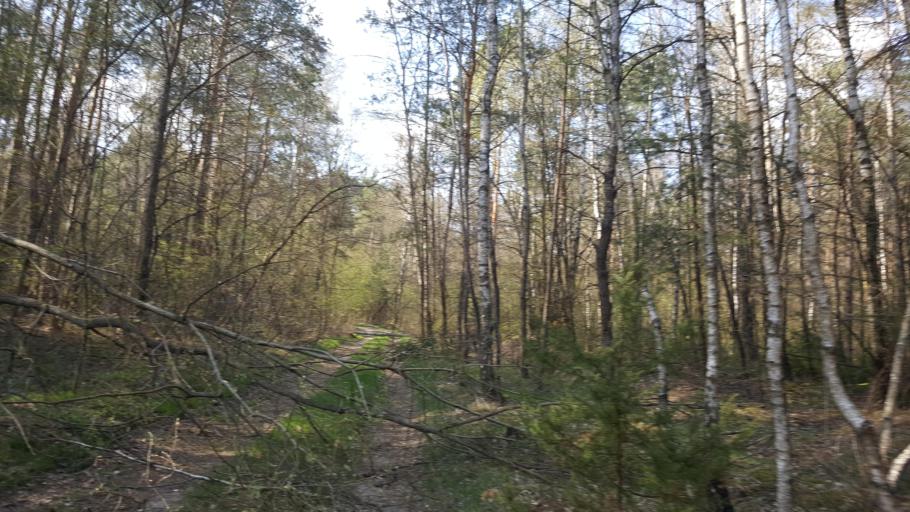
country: BY
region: Brest
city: Kamyanyets
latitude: 52.3441
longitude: 23.8456
